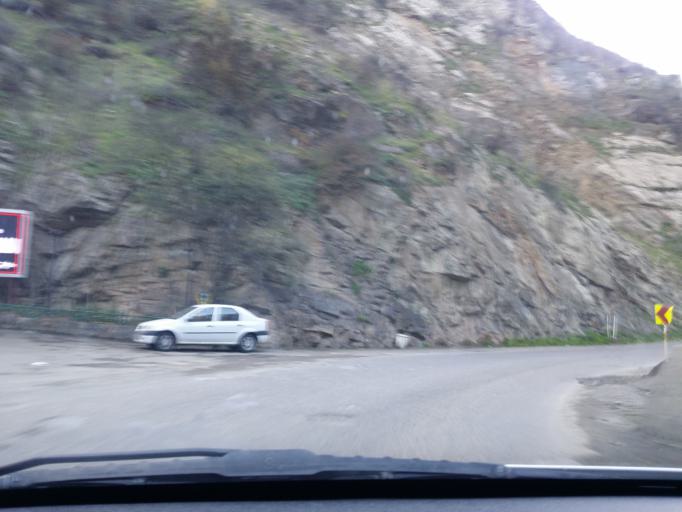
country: IR
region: Mazandaran
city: Chalus
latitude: 36.3009
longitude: 51.2485
